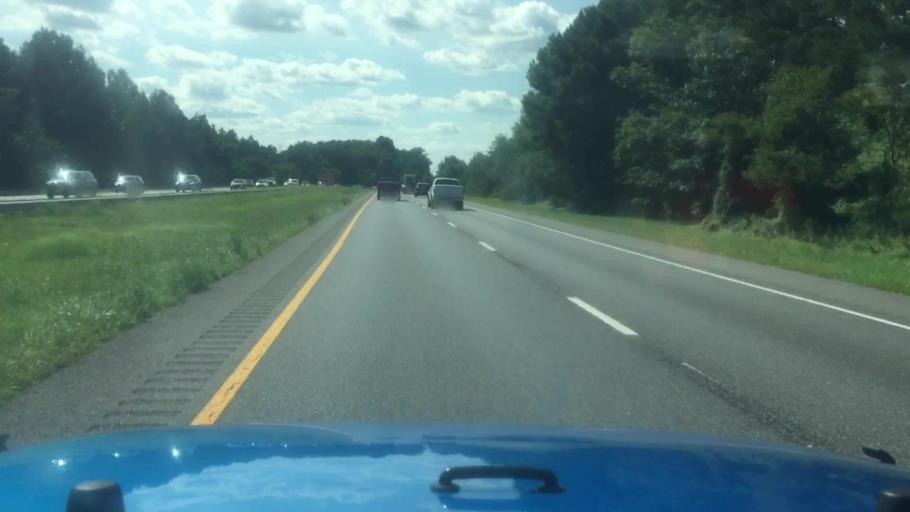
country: US
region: Maryland
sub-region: Anne Arundel County
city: Fort Meade
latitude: 39.0888
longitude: -76.7486
